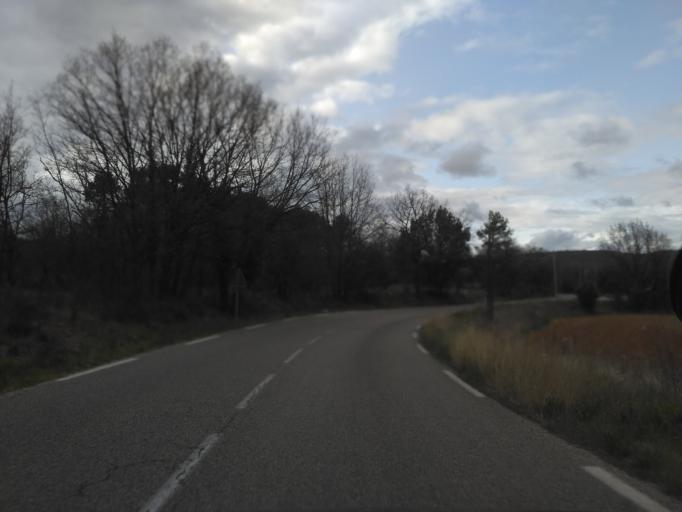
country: FR
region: Provence-Alpes-Cote d'Azur
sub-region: Departement du Var
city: Barjols
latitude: 43.5755
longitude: 6.0165
